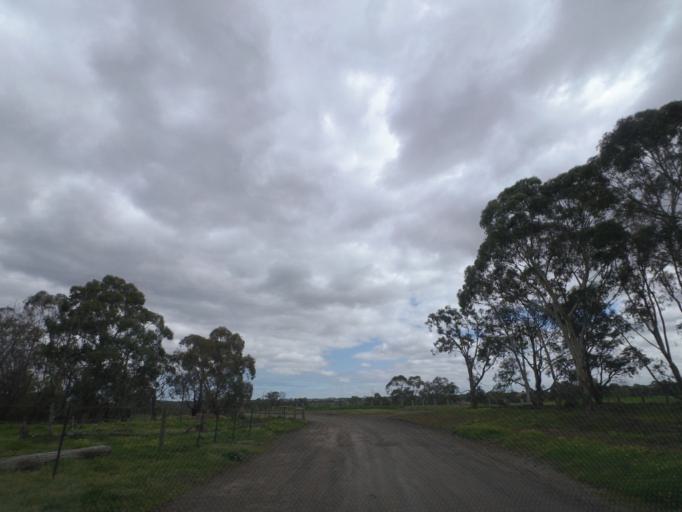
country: AU
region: Victoria
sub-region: Whittlesea
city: Mill Park
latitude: -37.6698
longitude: 145.0913
